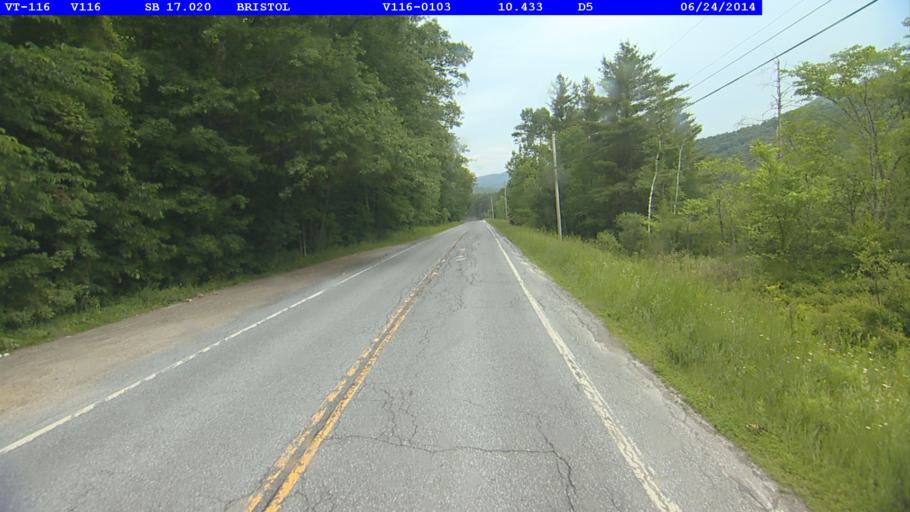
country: US
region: Vermont
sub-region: Addison County
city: Bristol
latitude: 44.1604
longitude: -73.0498
